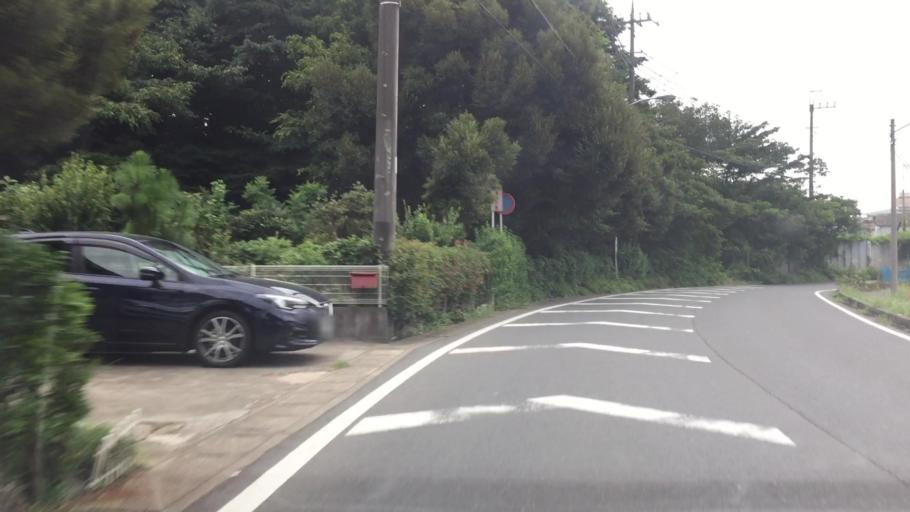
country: JP
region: Chiba
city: Kashiwa
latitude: 35.8076
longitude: 139.9504
